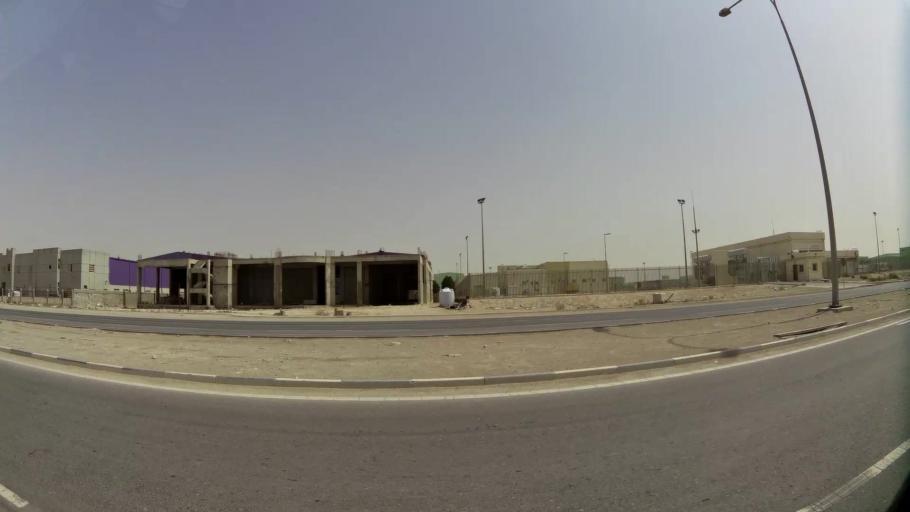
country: QA
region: Al Wakrah
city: Al Wukayr
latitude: 25.1606
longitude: 51.4076
